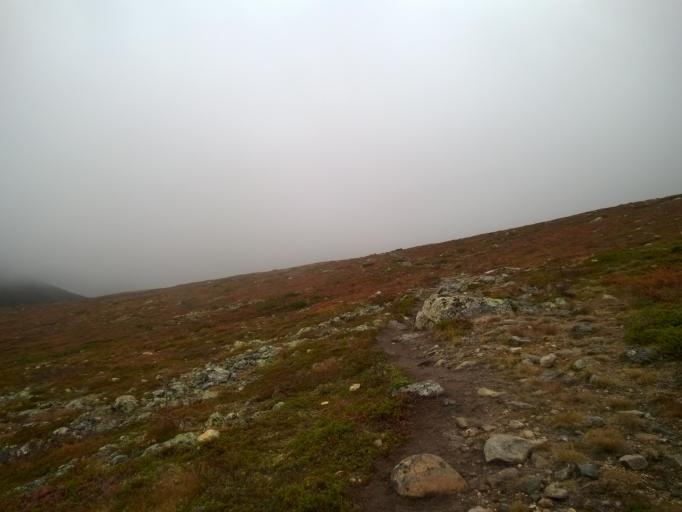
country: FI
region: Lapland
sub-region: Tunturi-Lappi
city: Muonio
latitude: 68.0553
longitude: 24.0826
